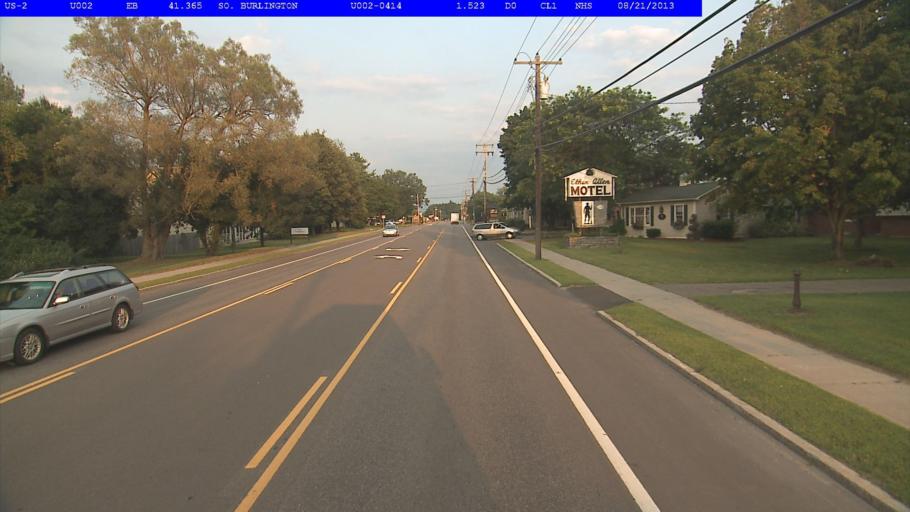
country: US
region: Vermont
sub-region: Chittenden County
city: South Burlington
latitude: 44.4648
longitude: -73.1616
